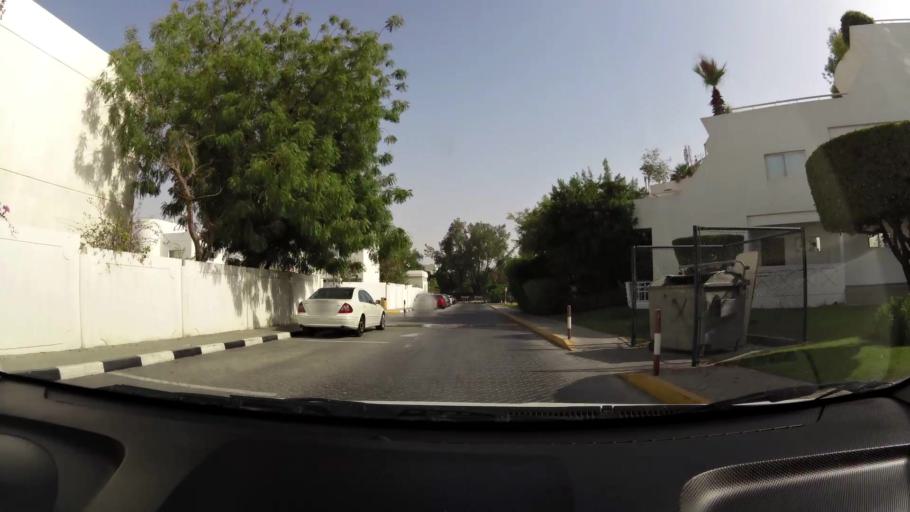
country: AE
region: Ash Shariqah
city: Sharjah
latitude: 25.2452
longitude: 55.3456
